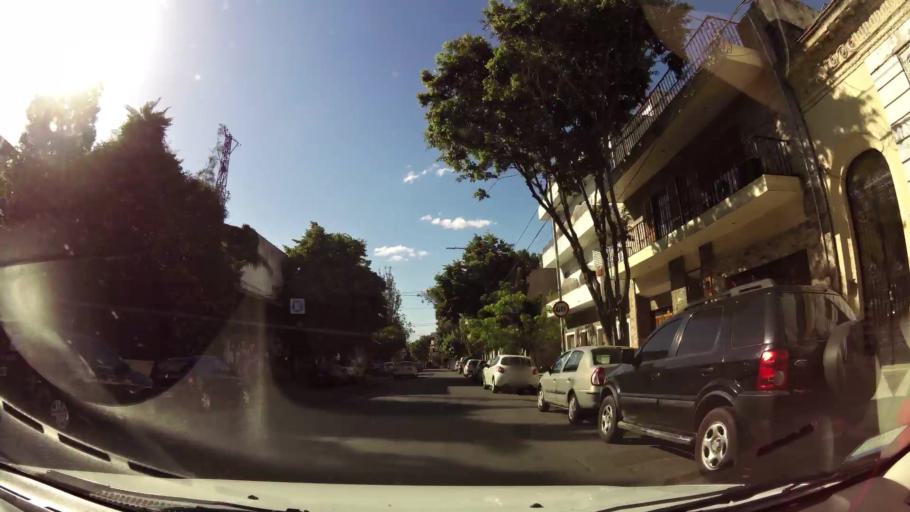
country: AR
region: Buenos Aires F.D.
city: Villa Santa Rita
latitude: -34.6170
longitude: -58.4635
